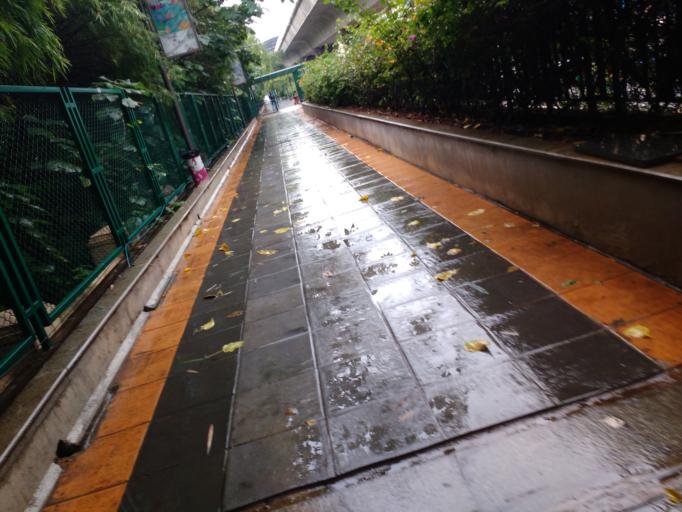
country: IN
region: Karnataka
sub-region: Bangalore Urban
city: Bangalore
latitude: 12.9762
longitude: 77.6042
